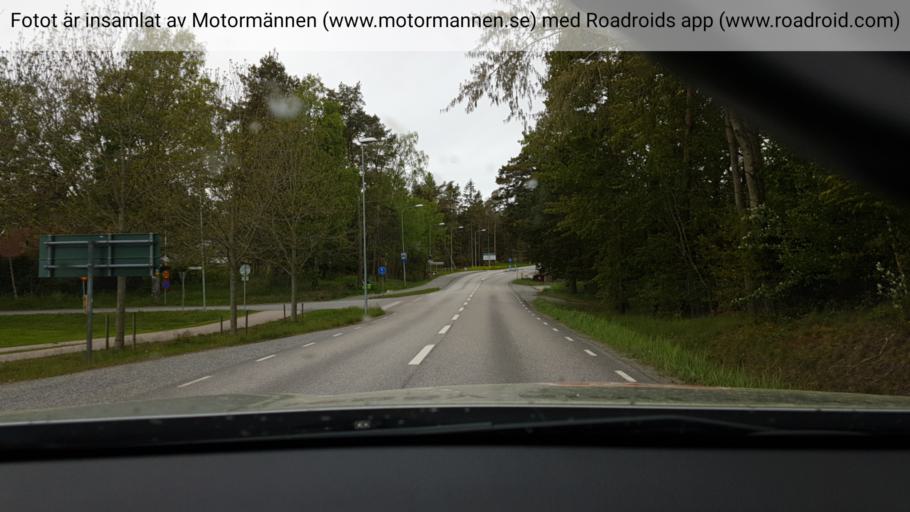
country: SE
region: Stockholm
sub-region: Varmdo Kommun
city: Holo
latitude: 59.2875
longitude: 18.6889
